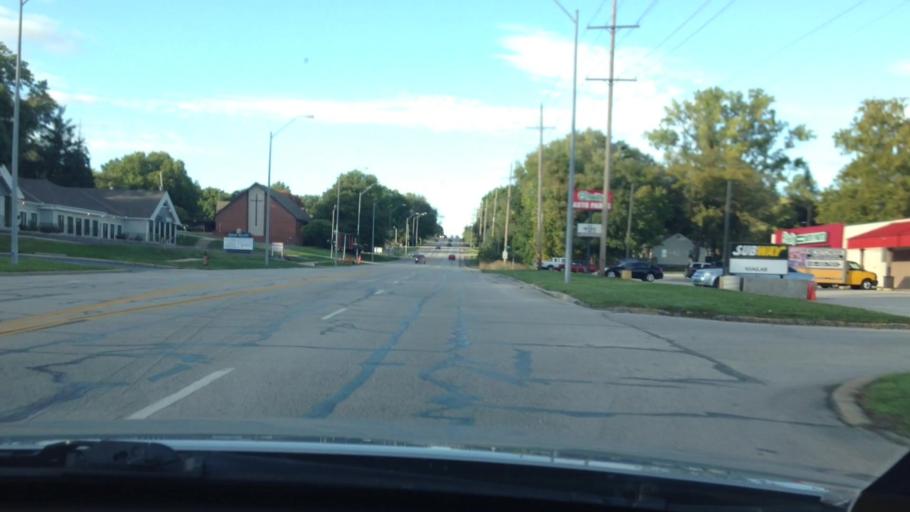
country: US
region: Missouri
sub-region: Platte County
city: Riverside
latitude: 39.1708
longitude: -94.5767
